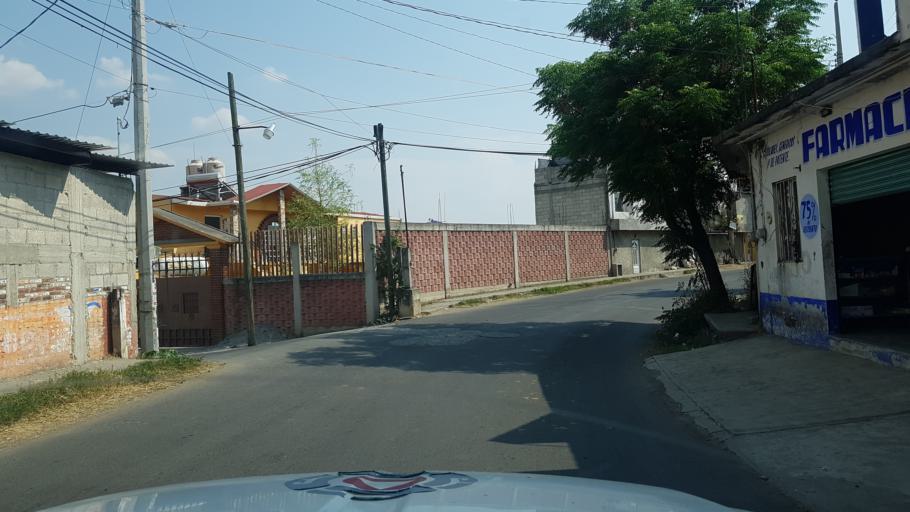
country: MX
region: Morelos
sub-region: Yecapixtla
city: Yecapixtla
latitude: 18.8887
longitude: -98.8637
